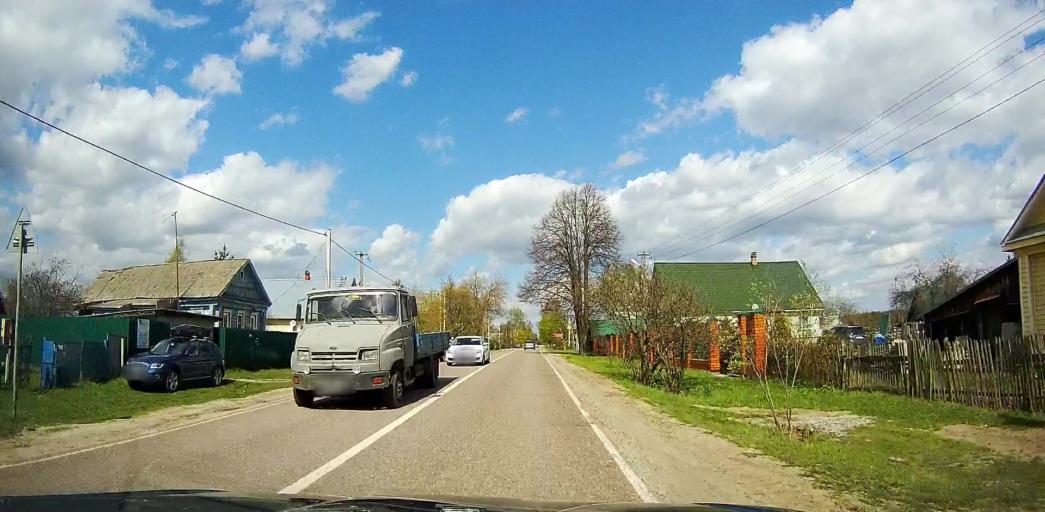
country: RU
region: Moskovskaya
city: Davydovo
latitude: 55.5750
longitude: 38.8204
